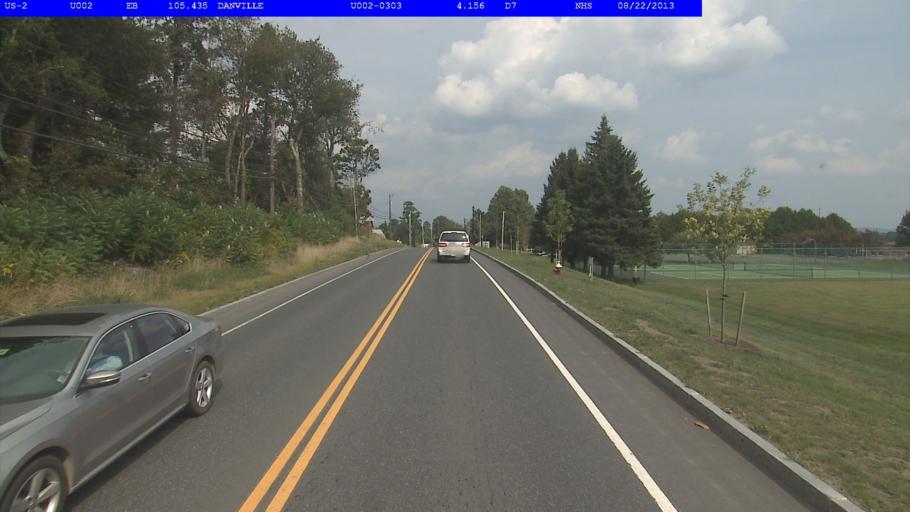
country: US
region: Vermont
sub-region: Caledonia County
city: Saint Johnsbury
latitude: 44.4113
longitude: -72.1462
